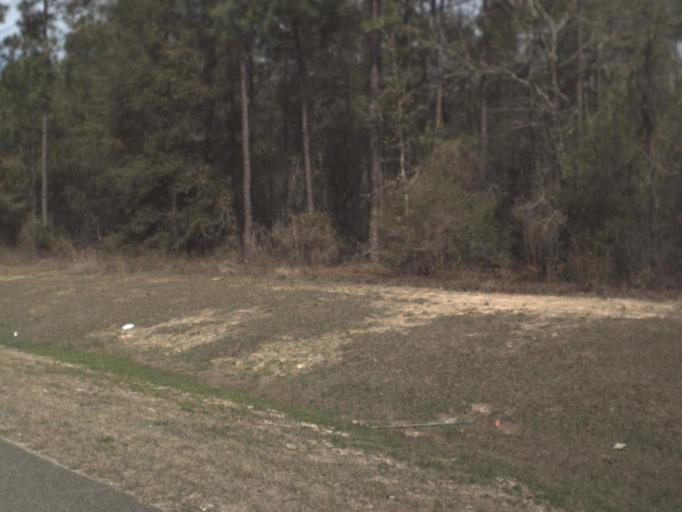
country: US
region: Florida
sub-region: Leon County
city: Tallahassee
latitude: 30.3852
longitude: -84.3101
